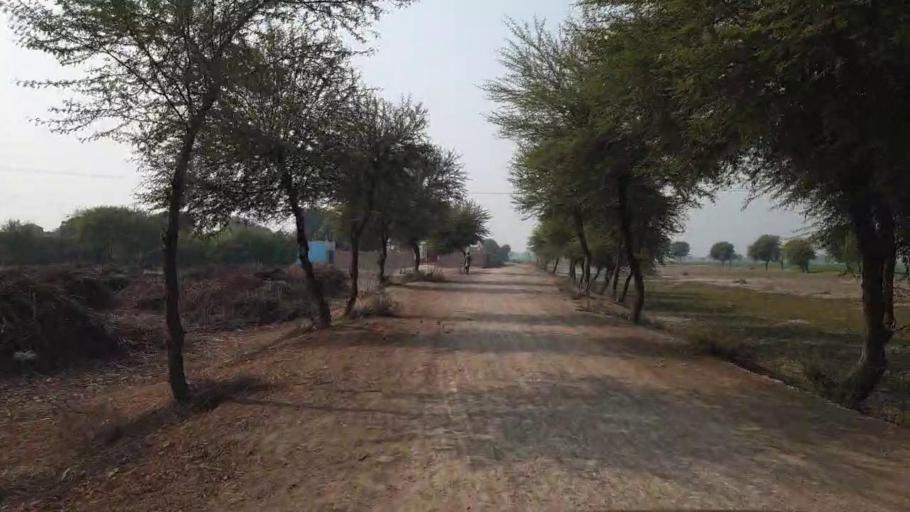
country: PK
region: Sindh
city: Hala
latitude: 25.8465
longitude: 68.4411
